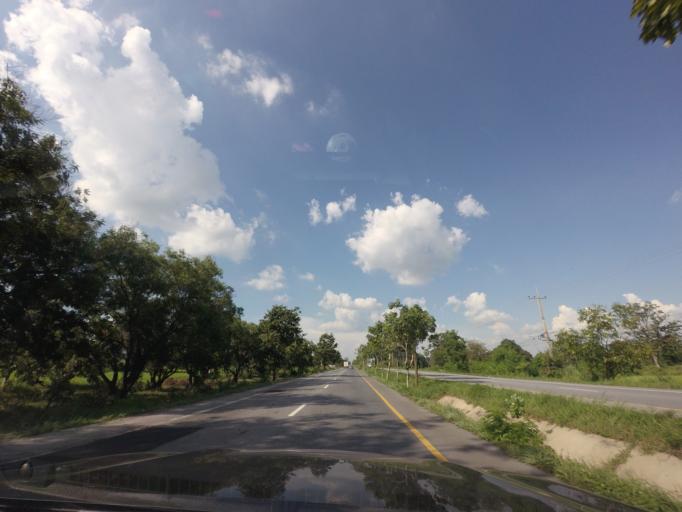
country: TH
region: Nakhon Ratchasima
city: Bua Lai
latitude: 15.7115
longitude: 102.5881
